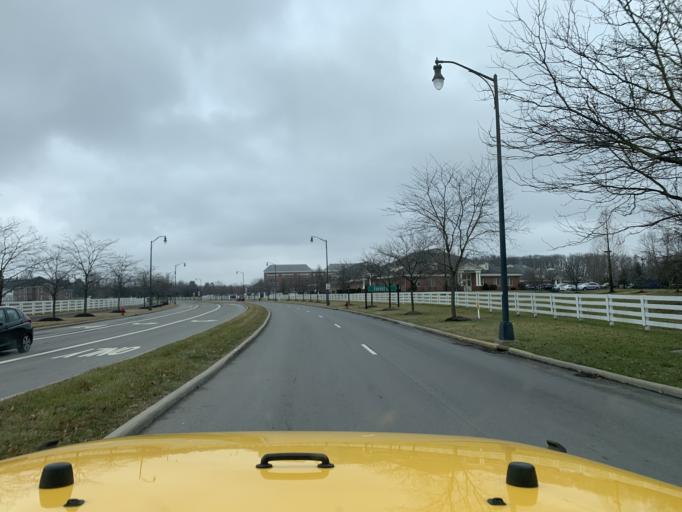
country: US
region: Ohio
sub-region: Franklin County
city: New Albany
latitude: 40.0901
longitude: -82.7933
